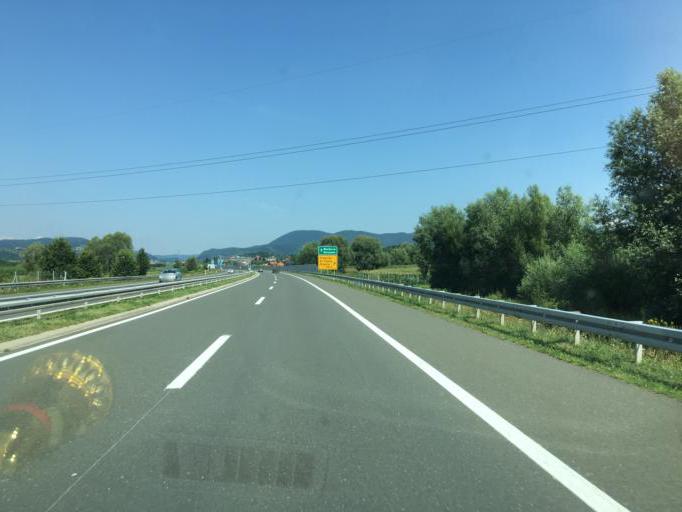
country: HR
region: Krapinsko-Zagorska
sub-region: Grad Krapina
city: Krapina
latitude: 46.1219
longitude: 15.8910
